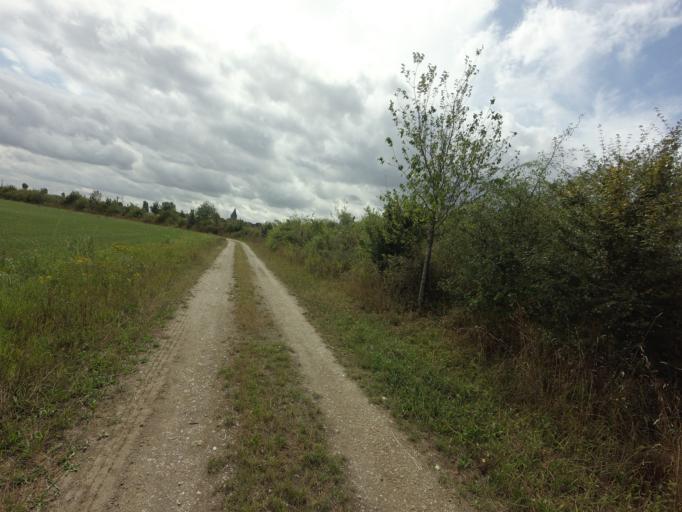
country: BE
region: Flanders
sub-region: Provincie Limburg
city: Maaseik
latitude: 51.1159
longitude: 5.8317
